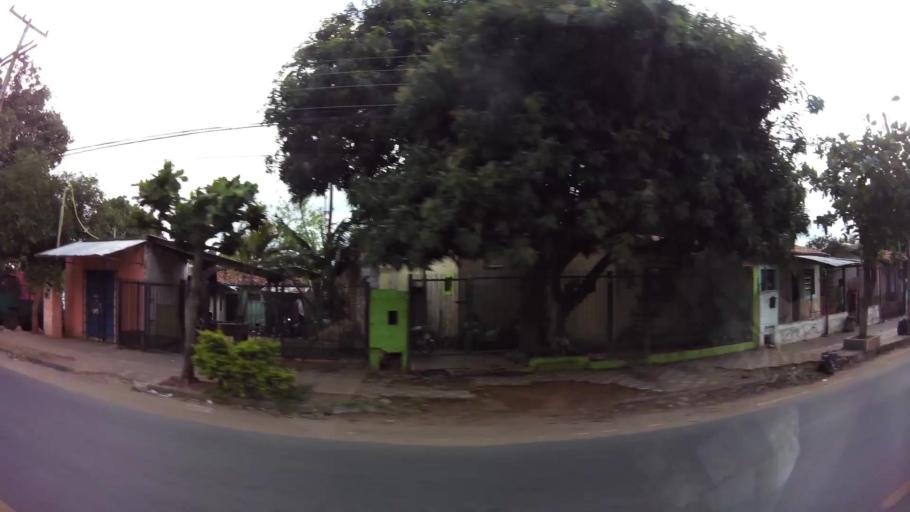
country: PY
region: Central
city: Villa Elisa
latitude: -25.3565
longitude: -57.5647
